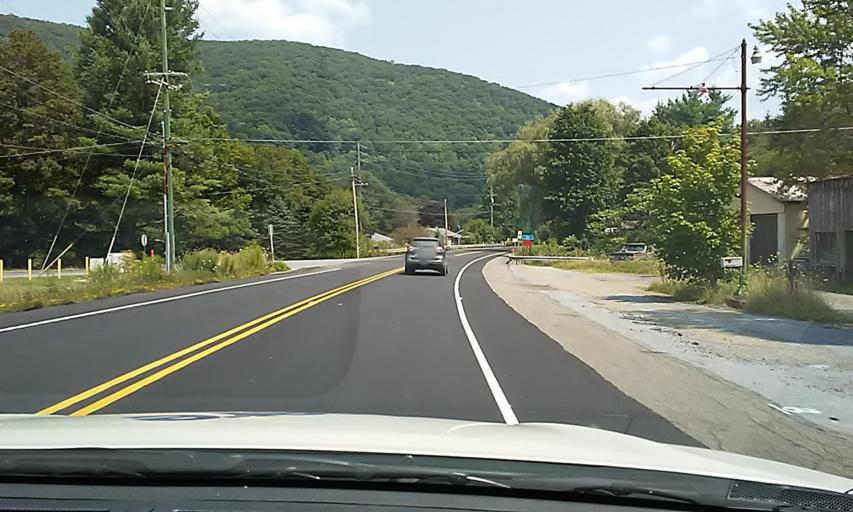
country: US
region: Pennsylvania
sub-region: Cameron County
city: Emporium
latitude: 41.4769
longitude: -78.3696
